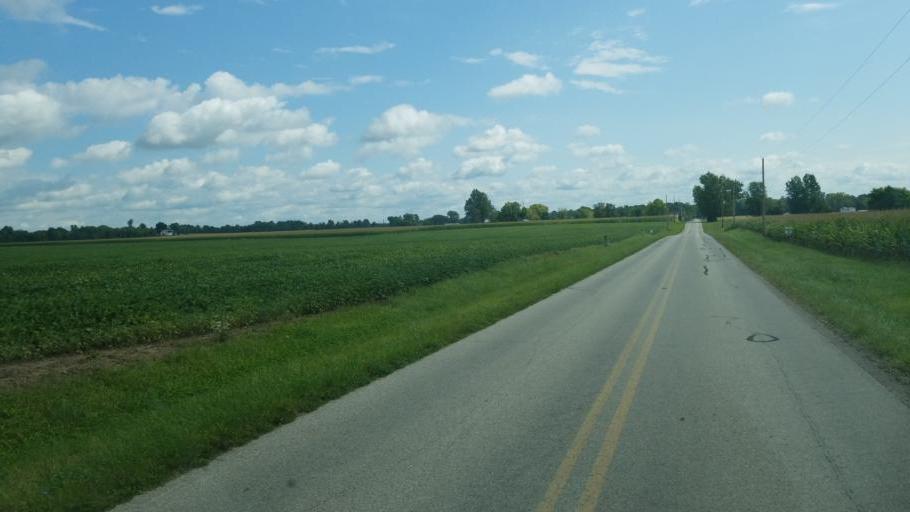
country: US
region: Ohio
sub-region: Seneca County
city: Tiffin
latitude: 41.0665
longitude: -83.0248
